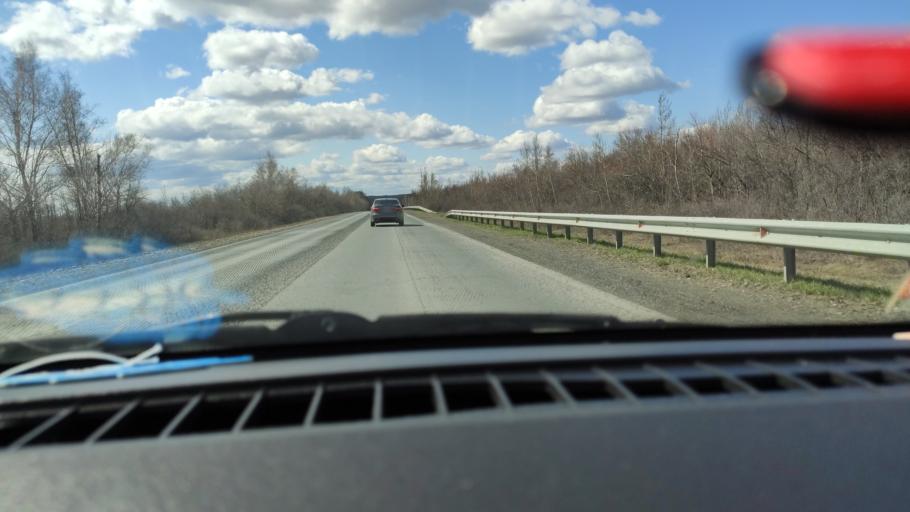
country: RU
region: Saratov
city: Dukhovnitskoye
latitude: 52.6707
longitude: 48.2215
